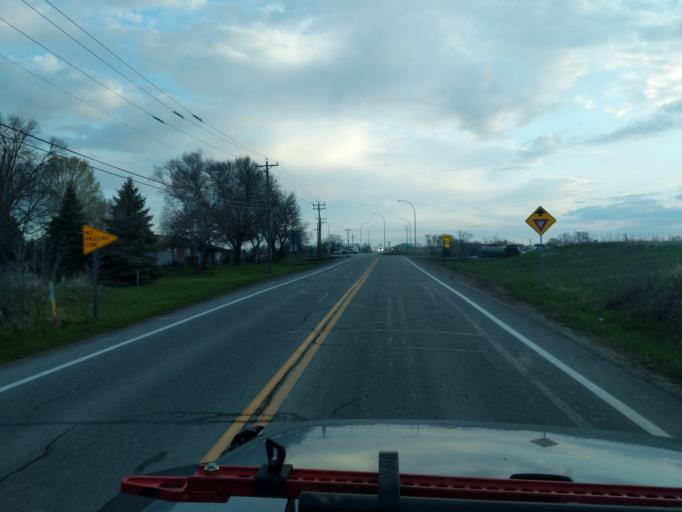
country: US
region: Minnesota
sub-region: Hennepin County
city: Rogers
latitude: 45.1609
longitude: -93.5216
